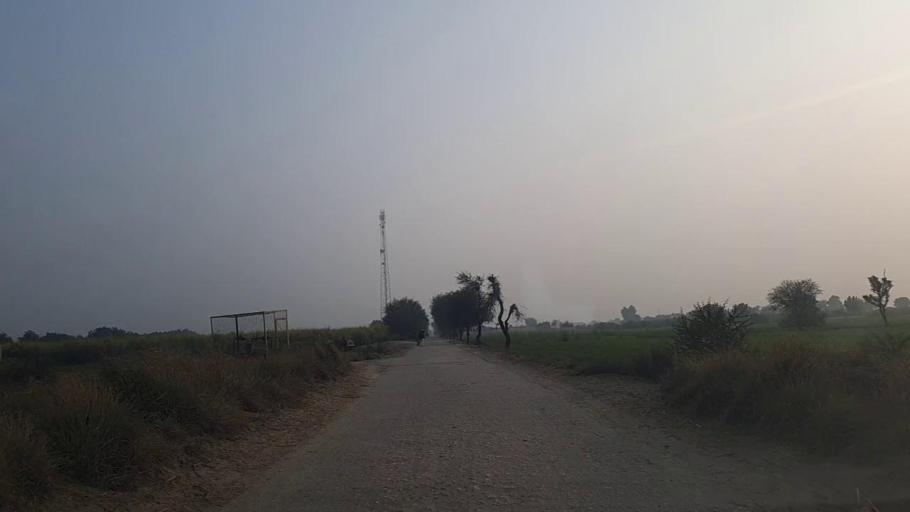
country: PK
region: Sindh
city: Khadro
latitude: 26.1239
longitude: 68.7959
